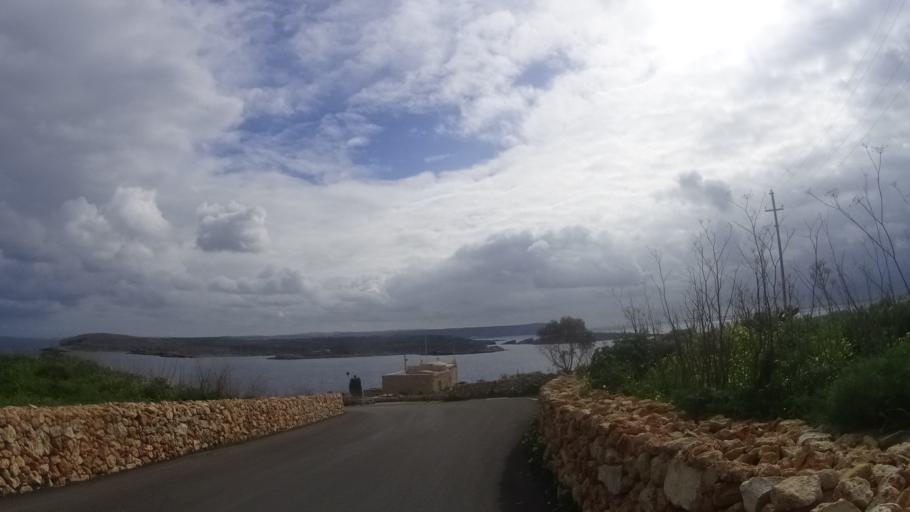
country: MT
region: Il-Qala
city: Qala
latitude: 36.0298
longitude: 14.3212
